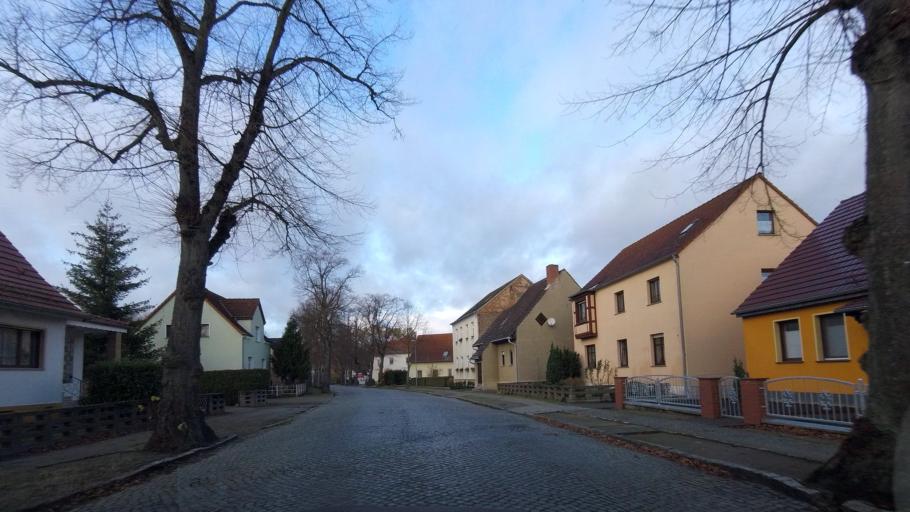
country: DE
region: Brandenburg
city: Treuenbrietzen
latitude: 52.0914
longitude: 12.8738
